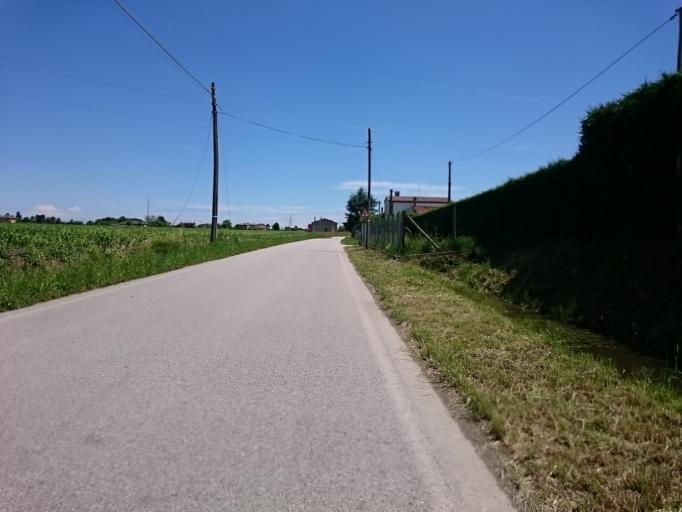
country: IT
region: Veneto
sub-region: Provincia di Padova
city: Campagnola
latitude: 45.2687
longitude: 12.0022
